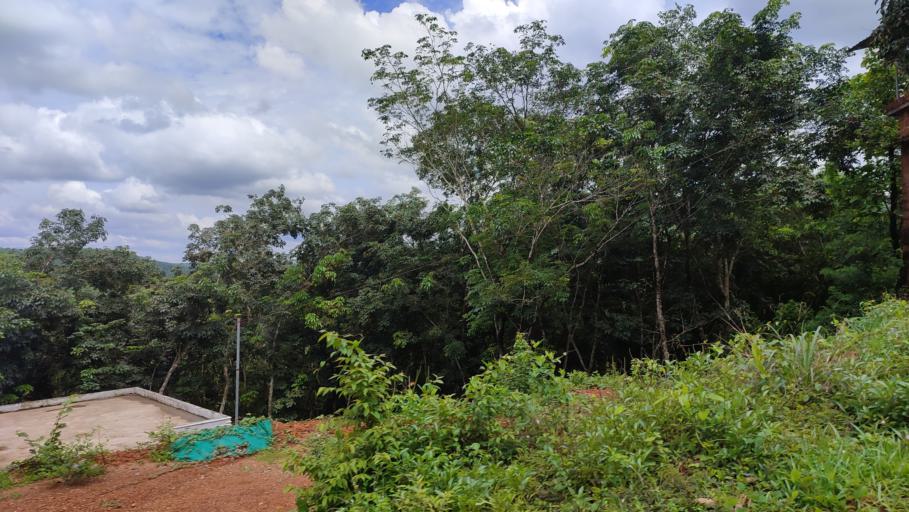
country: IN
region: Kerala
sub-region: Kasaragod District
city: Nileshwar
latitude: 12.2831
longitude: 75.2632
